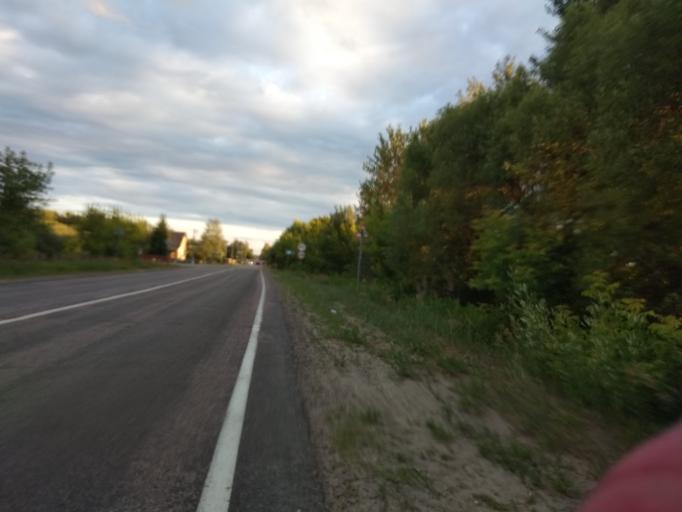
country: RU
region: Moskovskaya
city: Misheronskiy
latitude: 55.6034
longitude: 39.7076
